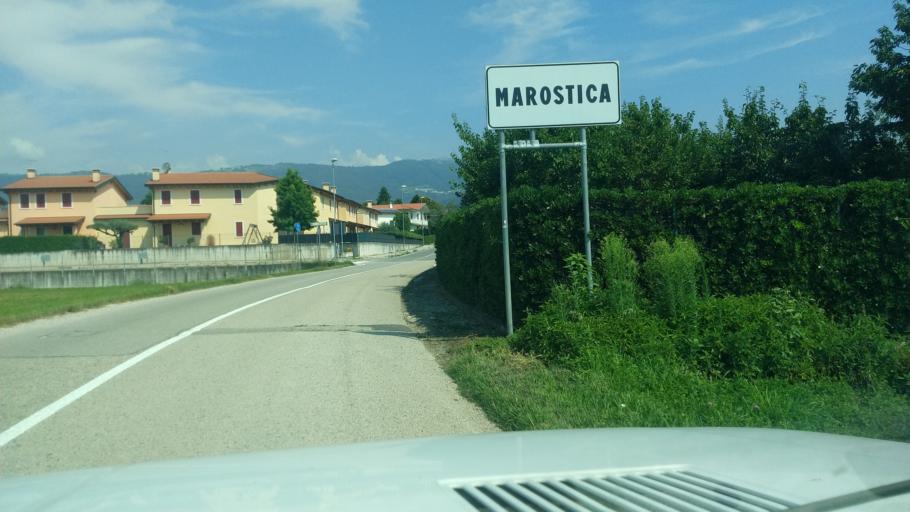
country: IT
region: Veneto
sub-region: Provincia di Vicenza
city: Marostica
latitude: 45.7431
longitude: 11.6692
